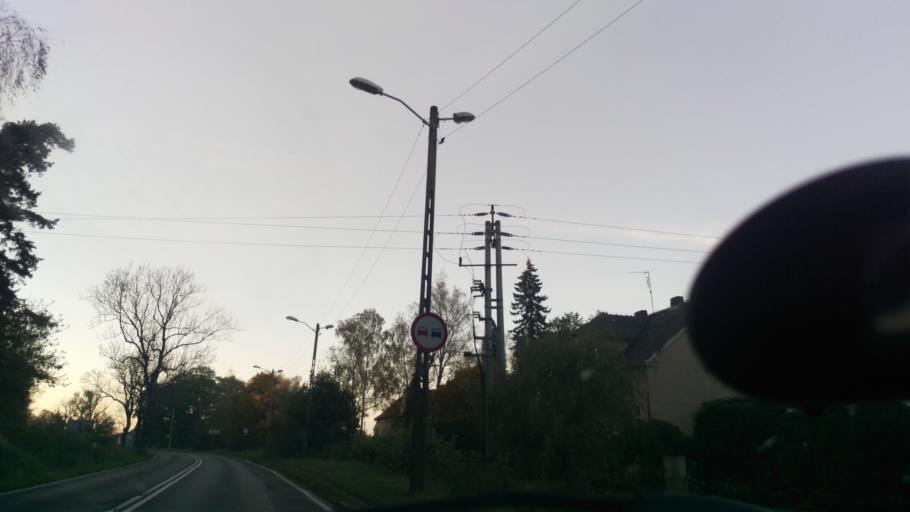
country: PL
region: West Pomeranian Voivodeship
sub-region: Powiat gryfinski
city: Stare Czarnowo
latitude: 53.3417
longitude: 14.7595
